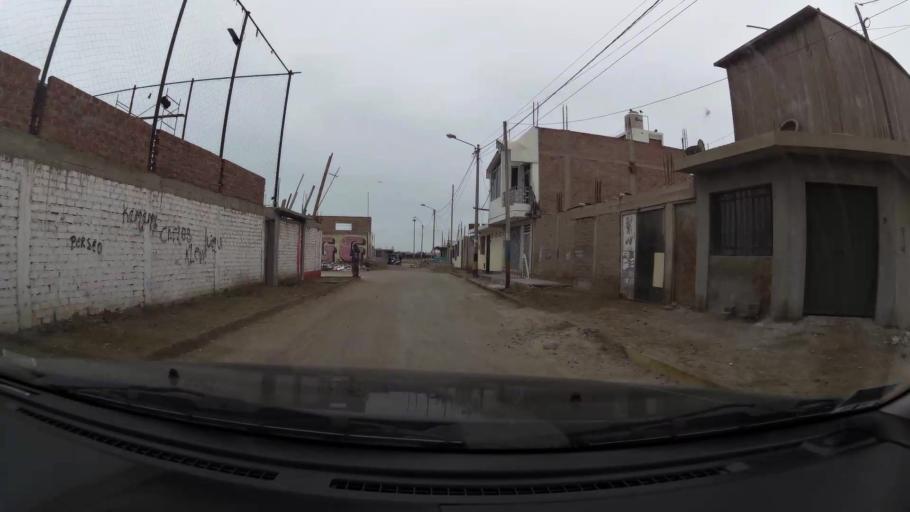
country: PE
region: Ica
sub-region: Provincia de Pisco
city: Pisco
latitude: -13.7296
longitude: -76.2202
